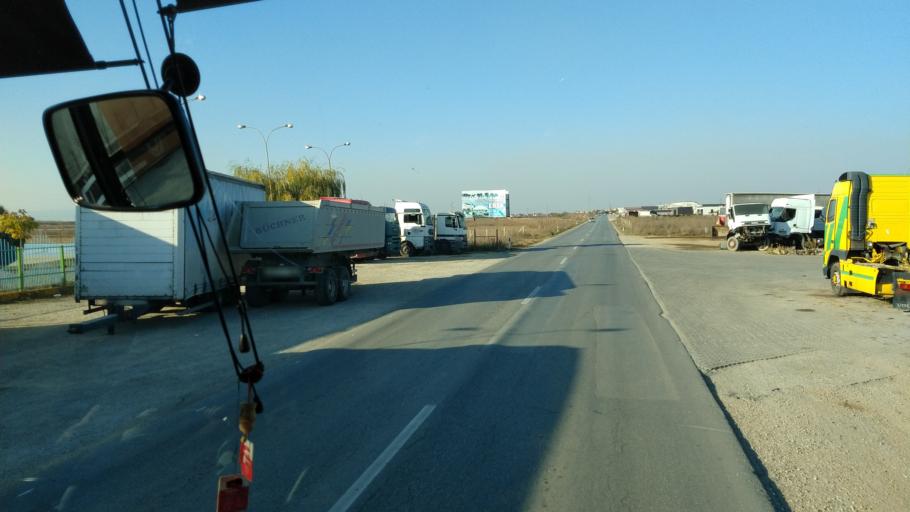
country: XK
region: Pristina
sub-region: Lipjan
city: Lipljan
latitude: 42.5206
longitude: 21.1121
